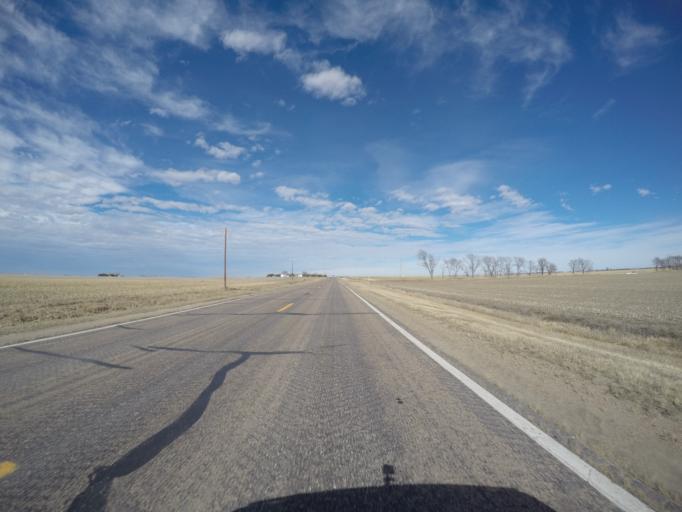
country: US
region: Nebraska
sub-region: Franklin County
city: Franklin
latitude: 40.2696
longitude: -98.9523
